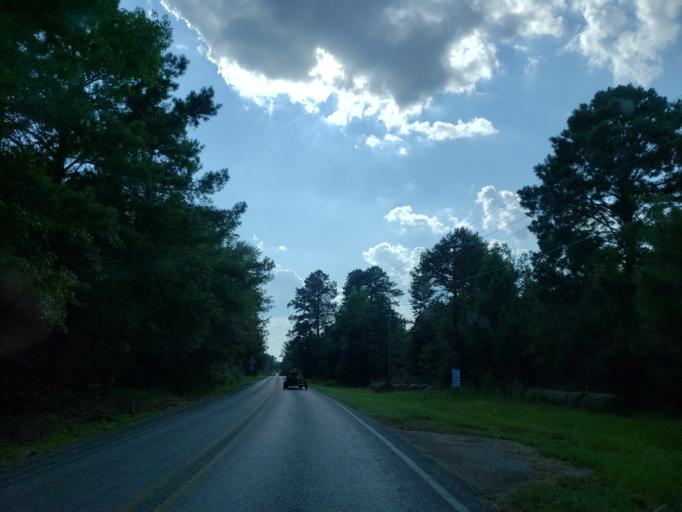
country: US
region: Mississippi
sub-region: Jones County
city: Sharon
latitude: 31.9198
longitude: -89.0213
